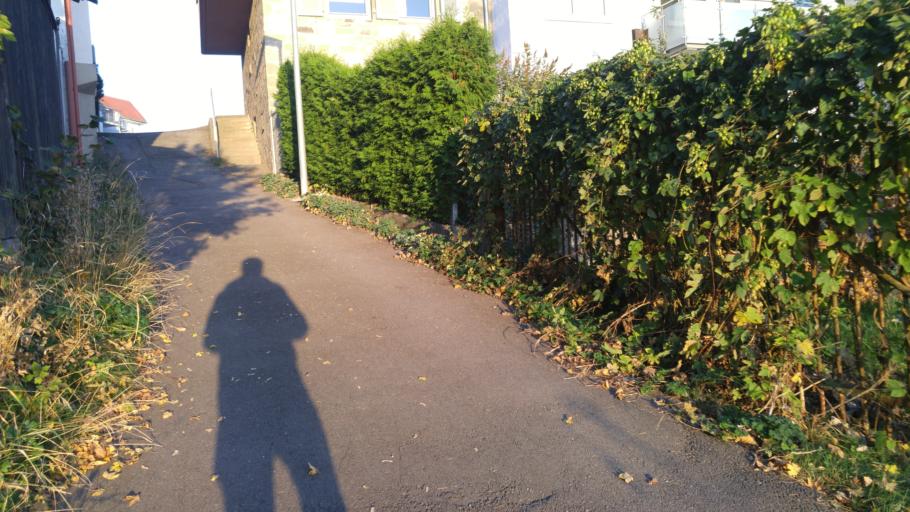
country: DE
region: Baden-Wuerttemberg
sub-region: Regierungsbezirk Stuttgart
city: Waldenburg
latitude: 49.1867
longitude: 9.6428
